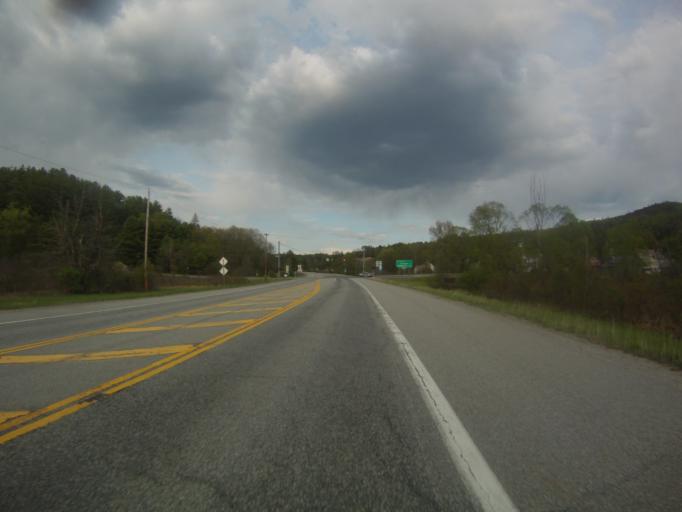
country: US
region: New York
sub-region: Warren County
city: Warrensburg
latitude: 43.6566
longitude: -73.8025
